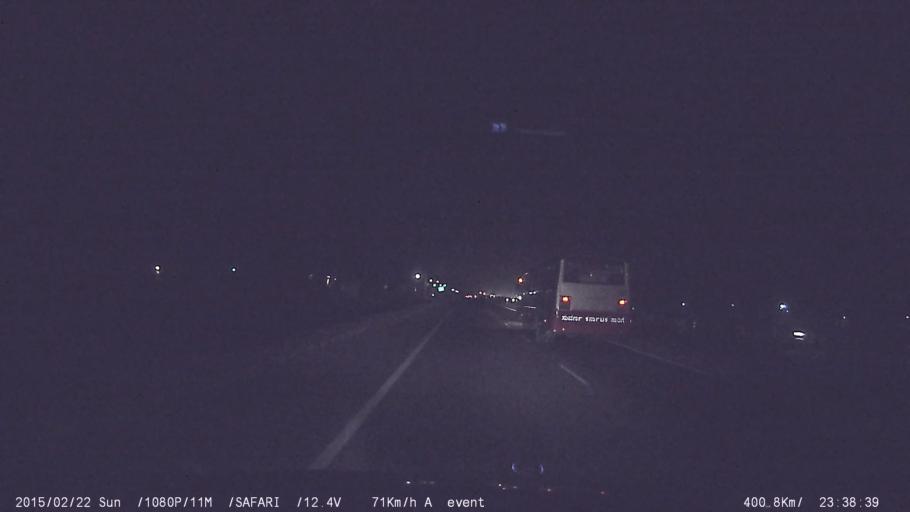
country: IN
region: Tamil Nadu
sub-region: Salem
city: Omalur
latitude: 11.7119
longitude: 78.0863
